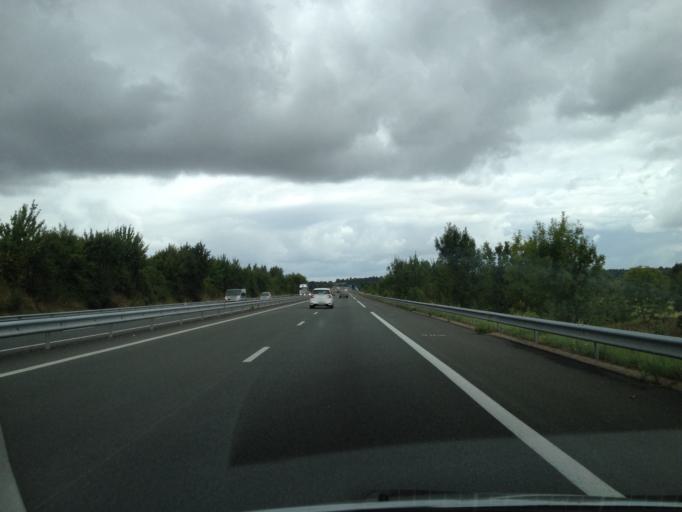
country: FR
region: Pays de la Loire
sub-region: Departement de la Vendee
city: Saint-Martin-des-Noyers
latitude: 46.7579
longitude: -1.1705
